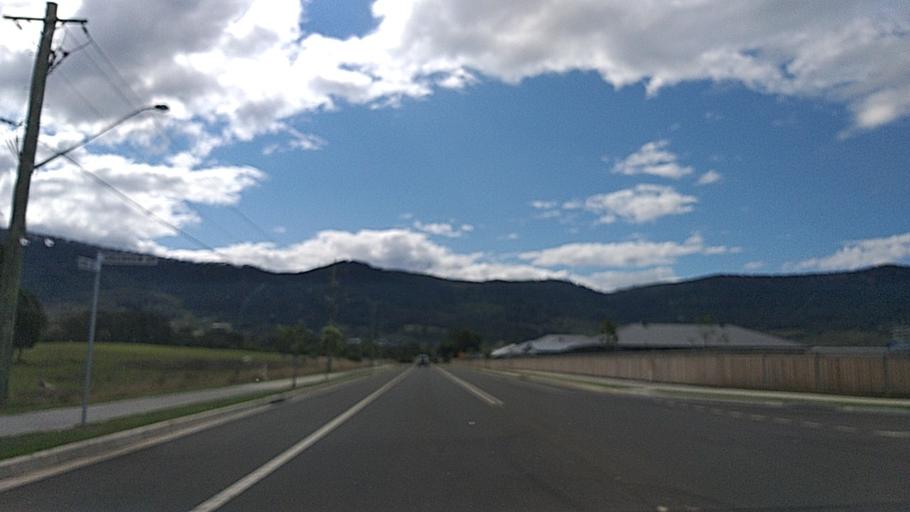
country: AU
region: New South Wales
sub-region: Wollongong
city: Dapto
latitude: -34.4832
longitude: 150.7676
